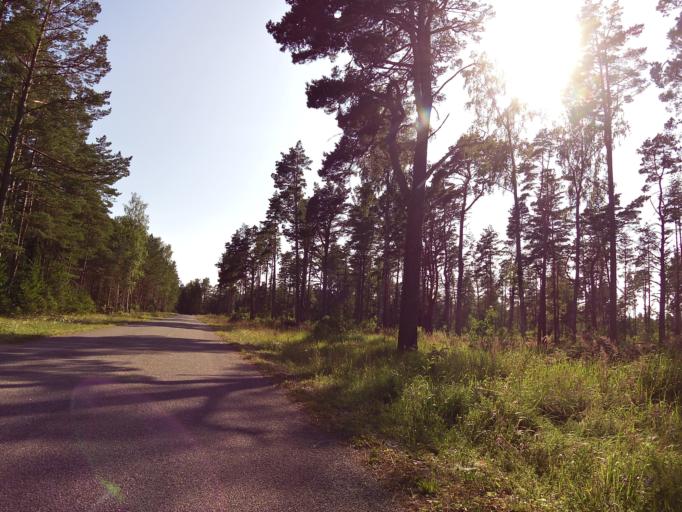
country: EE
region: Hiiumaa
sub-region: Kaerdla linn
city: Kardla
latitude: 58.8967
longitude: 22.2768
